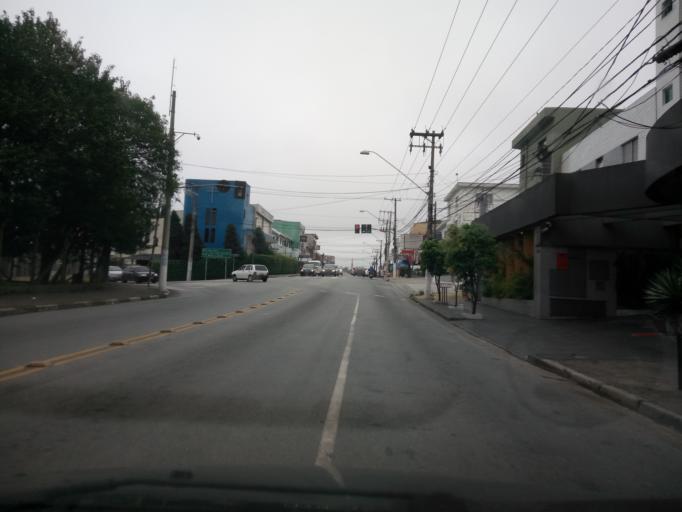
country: BR
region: Sao Paulo
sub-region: Sao Bernardo Do Campo
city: Sao Bernardo do Campo
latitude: -23.7297
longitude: -46.5672
